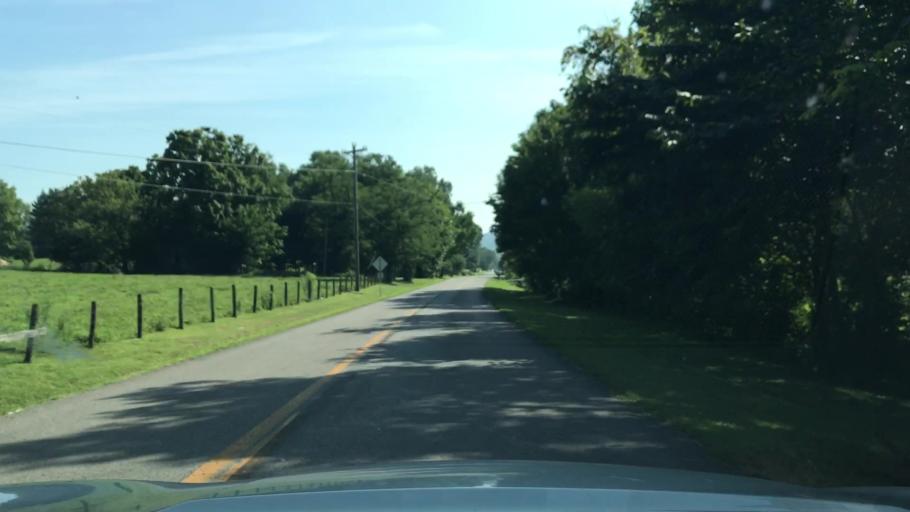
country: US
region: Kentucky
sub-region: Clinton County
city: Albany
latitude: 36.6824
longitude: -85.0637
